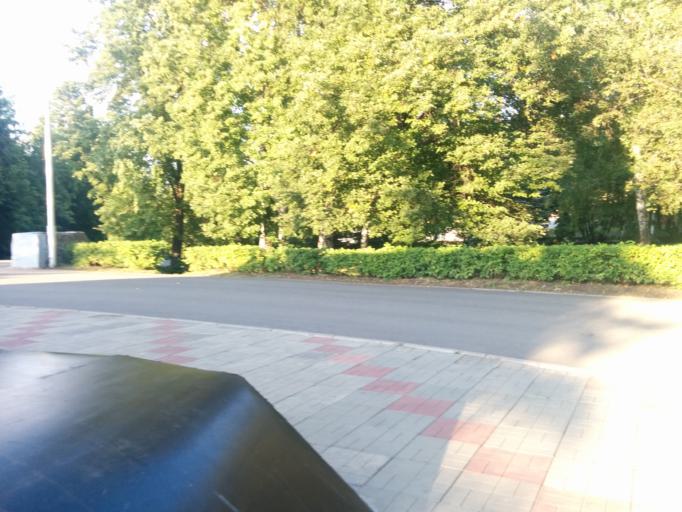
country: RU
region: Bashkortostan
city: Ufa
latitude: 54.8257
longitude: 56.0551
